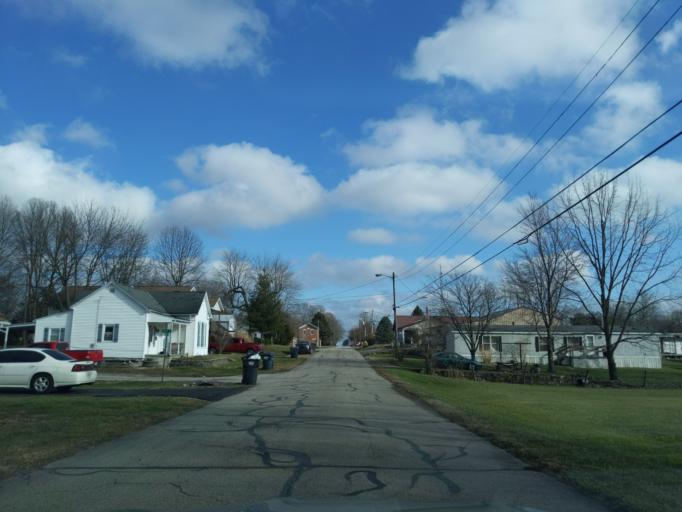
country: US
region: Indiana
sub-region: Ripley County
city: Batesville
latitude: 39.3093
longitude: -85.3283
